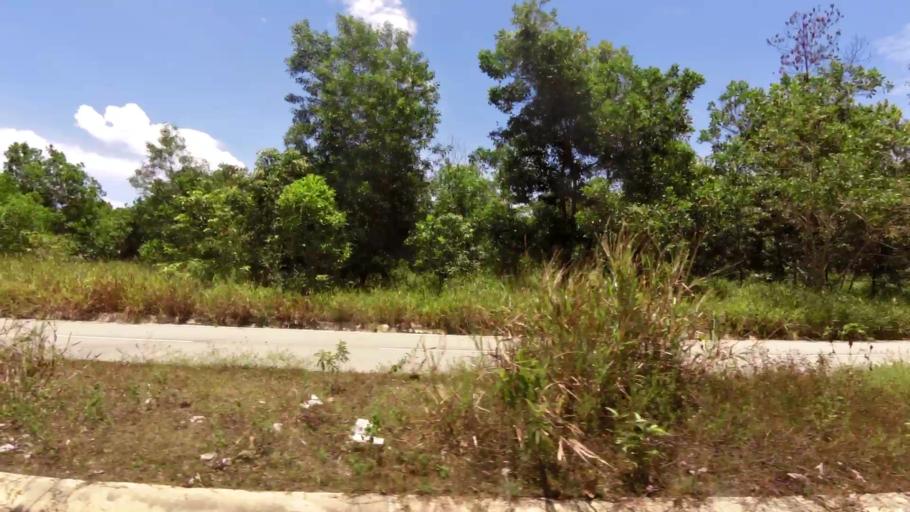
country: BN
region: Brunei and Muara
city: Bandar Seri Begawan
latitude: 4.9414
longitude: 114.8827
